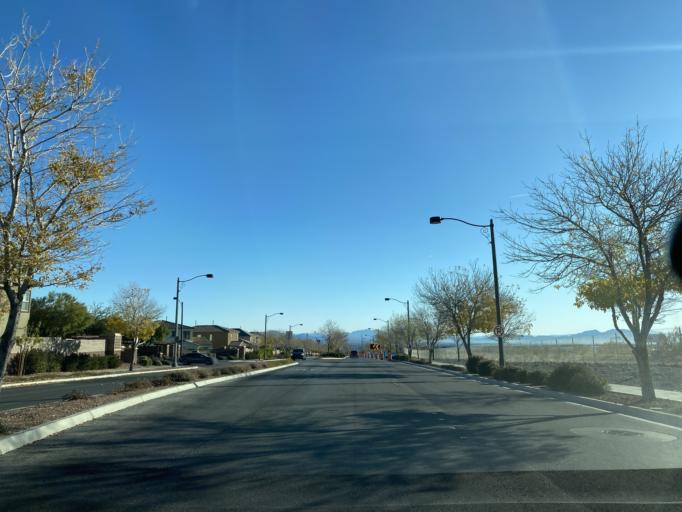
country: US
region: Nevada
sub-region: Clark County
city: Summerlin South
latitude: 36.2992
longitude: -115.3250
